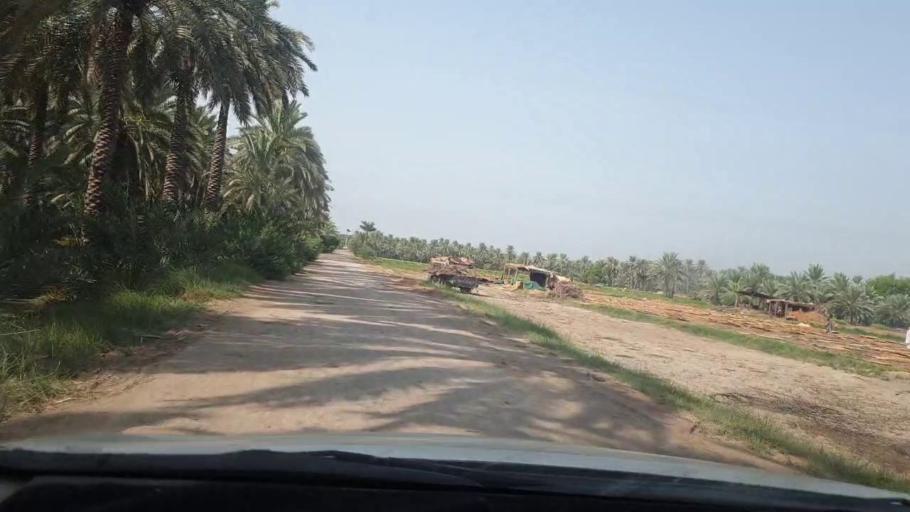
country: PK
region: Sindh
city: Rohri
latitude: 27.5966
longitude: 68.8673
